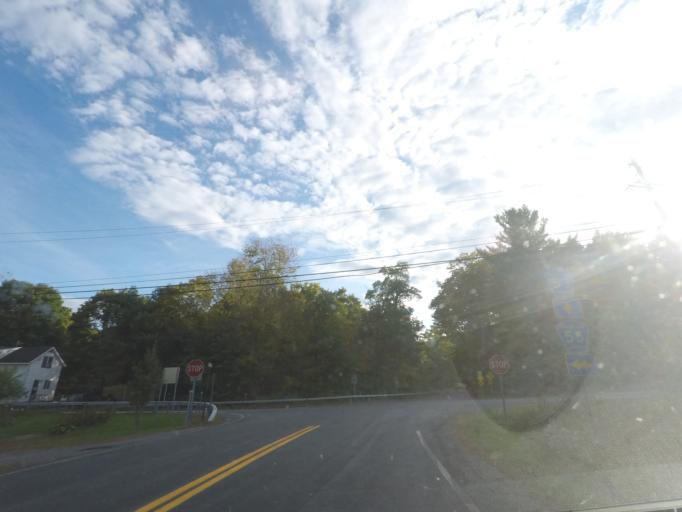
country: US
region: New York
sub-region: Rensselaer County
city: West Sand Lake
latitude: 42.6160
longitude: -73.6378
